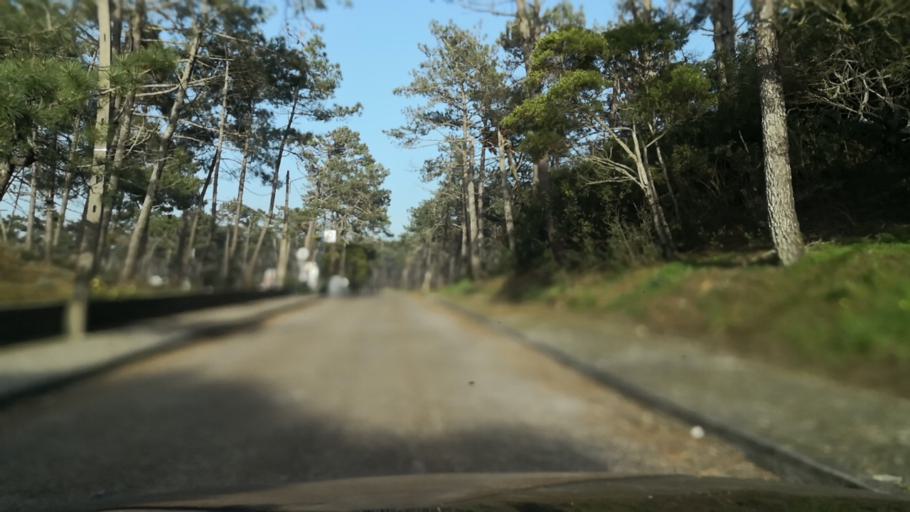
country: PT
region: Leiria
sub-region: Alcobaca
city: Pataias
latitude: 39.7575
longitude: -9.0268
